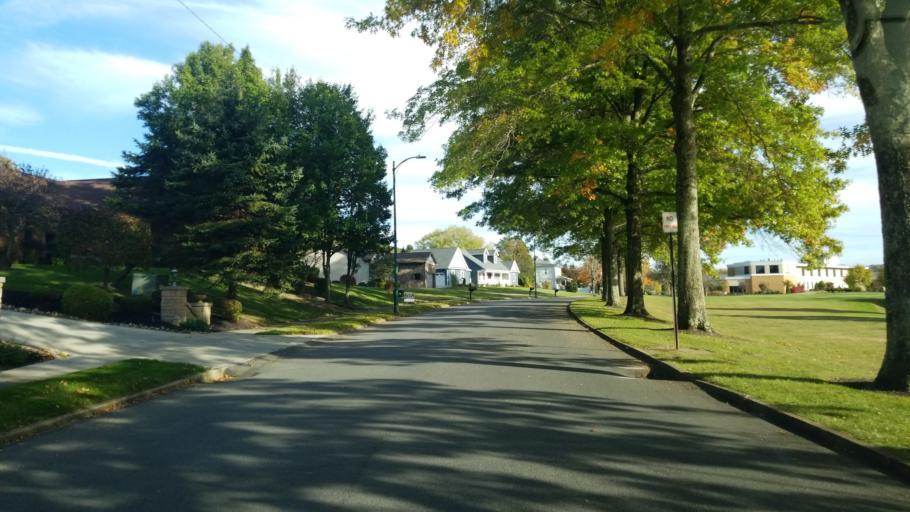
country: US
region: Pennsylvania
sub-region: Jefferson County
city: Brockway
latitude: 41.2525
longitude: -78.7924
